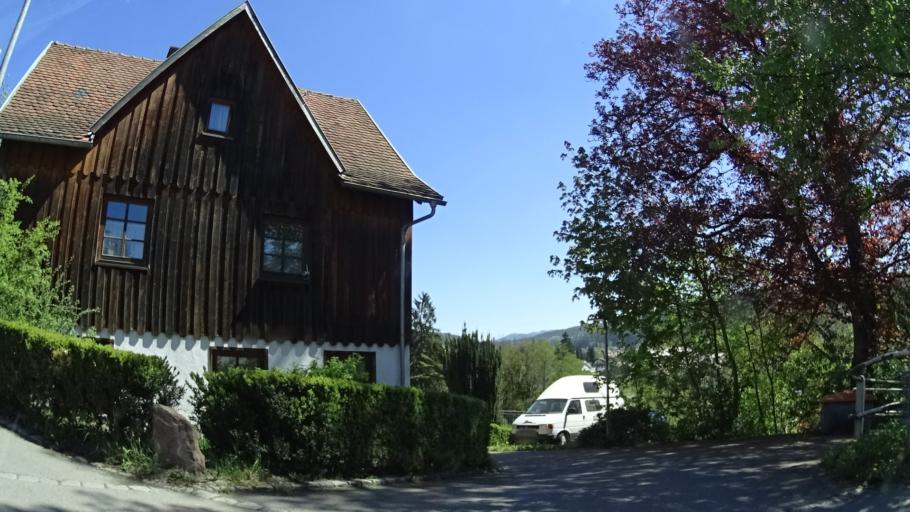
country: DE
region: Baden-Wuerttemberg
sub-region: Freiburg Region
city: Rottweil
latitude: 48.1591
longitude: 8.6410
